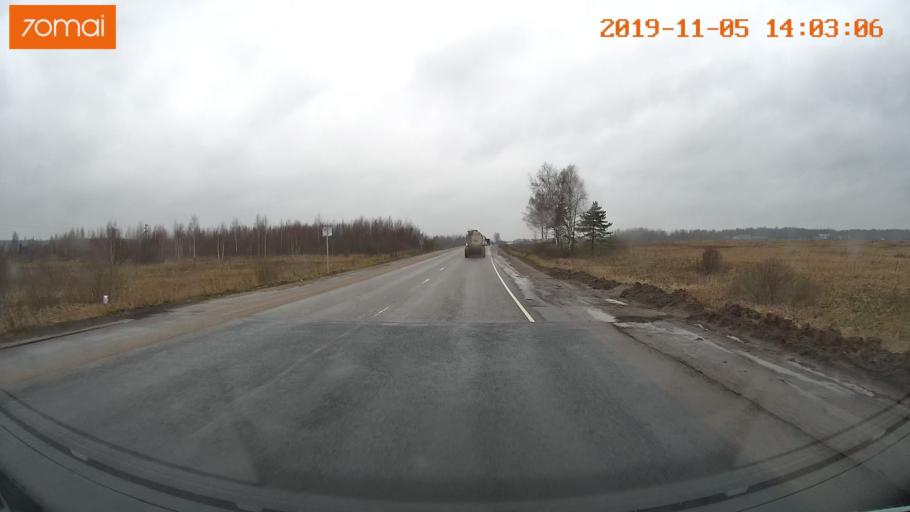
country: RU
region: Ivanovo
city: Kokhma
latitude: 56.9988
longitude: 41.2018
